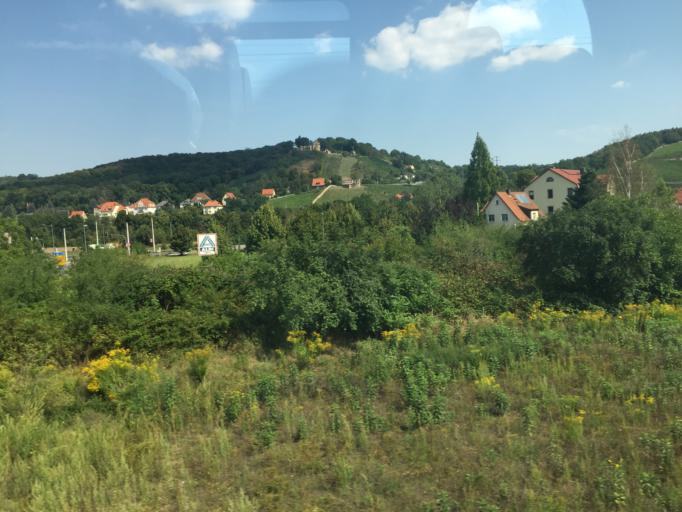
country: DE
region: Saxony
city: Coswig
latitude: 51.1134
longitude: 13.6109
